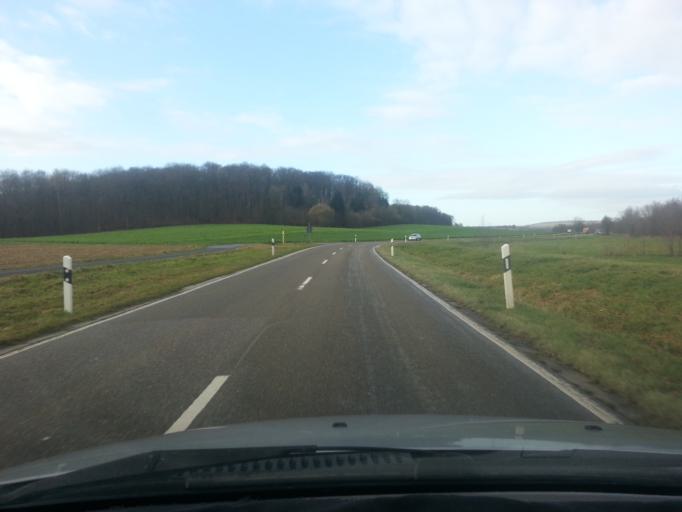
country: DE
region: Baden-Wuerttemberg
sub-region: Regierungsbezirk Stuttgart
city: Eppingen
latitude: 49.1542
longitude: 8.8894
